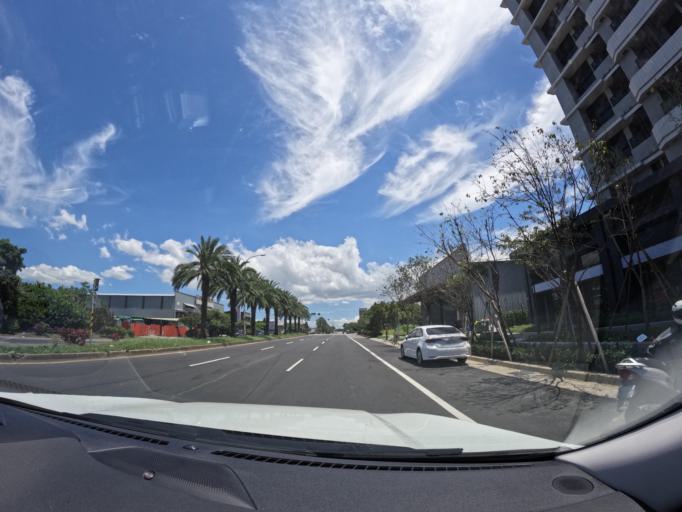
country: TW
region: Taipei
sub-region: Taipei
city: Banqiao
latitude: 25.0936
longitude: 121.3793
